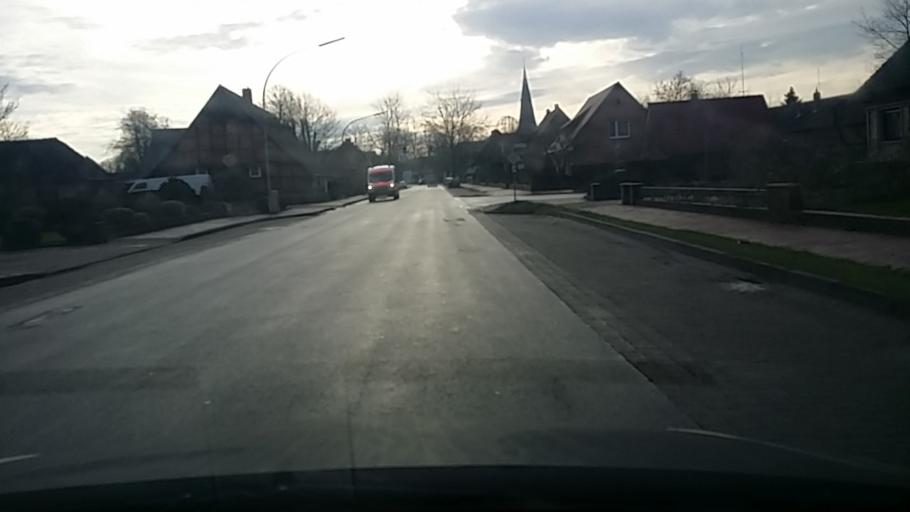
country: DE
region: Lower Saxony
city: Menslage
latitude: 52.6789
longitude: 7.8157
